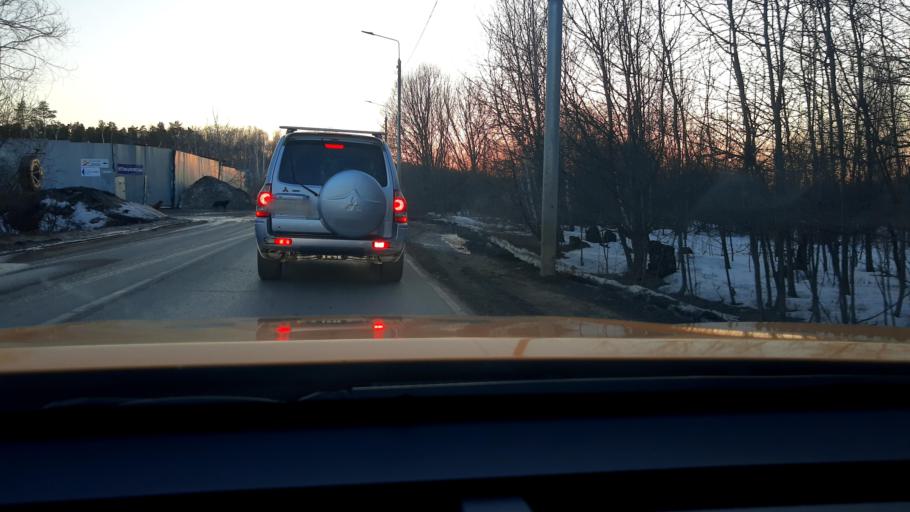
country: RU
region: Moskovskaya
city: Gorki-Leninskiye
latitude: 55.5243
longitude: 37.7445
